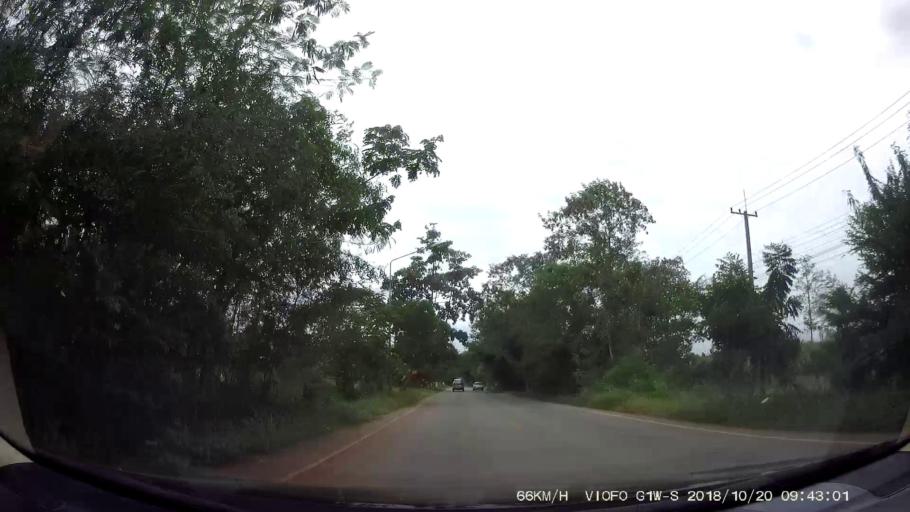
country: TH
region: Chaiyaphum
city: Khon San
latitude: 16.4693
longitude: 101.9500
